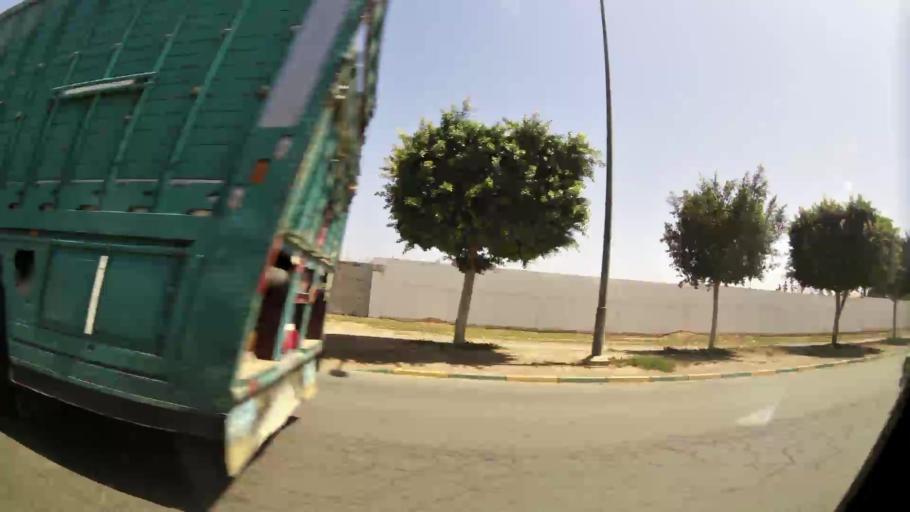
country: MA
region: Souss-Massa-Draa
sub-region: Inezgane-Ait Mellou
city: Inezgane
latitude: 30.3354
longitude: -9.4923
